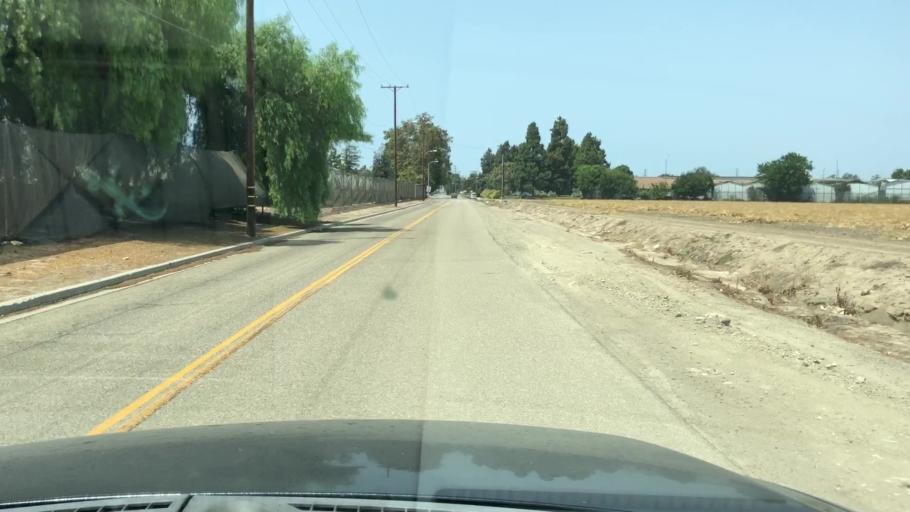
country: US
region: California
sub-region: Ventura County
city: Camarillo
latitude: 34.2052
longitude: -119.0044
